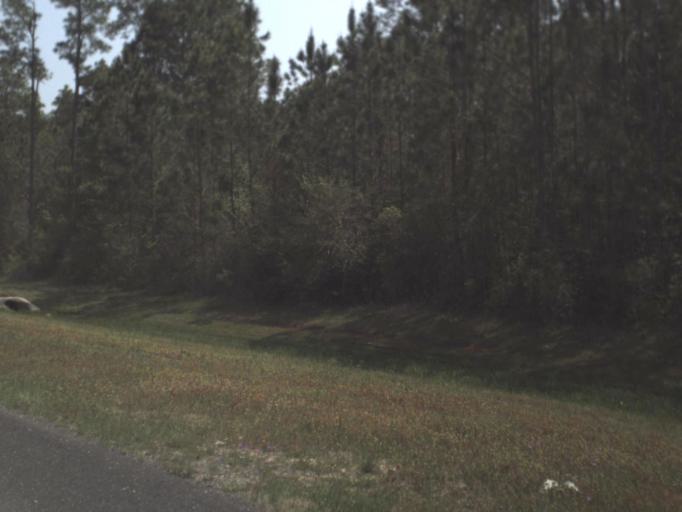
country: US
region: Florida
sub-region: Santa Rosa County
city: Bagdad
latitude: 30.5101
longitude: -87.0831
